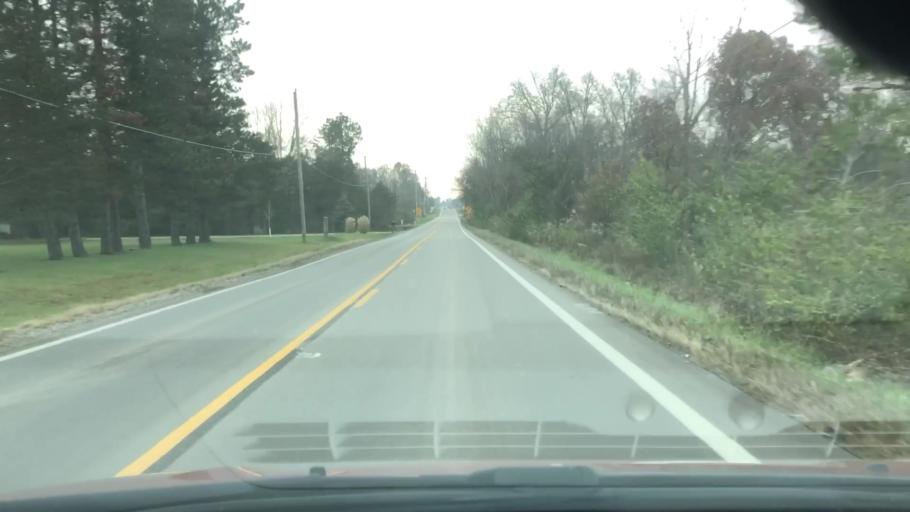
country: US
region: Ohio
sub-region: Franklin County
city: New Albany
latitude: 40.1156
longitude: -82.8111
